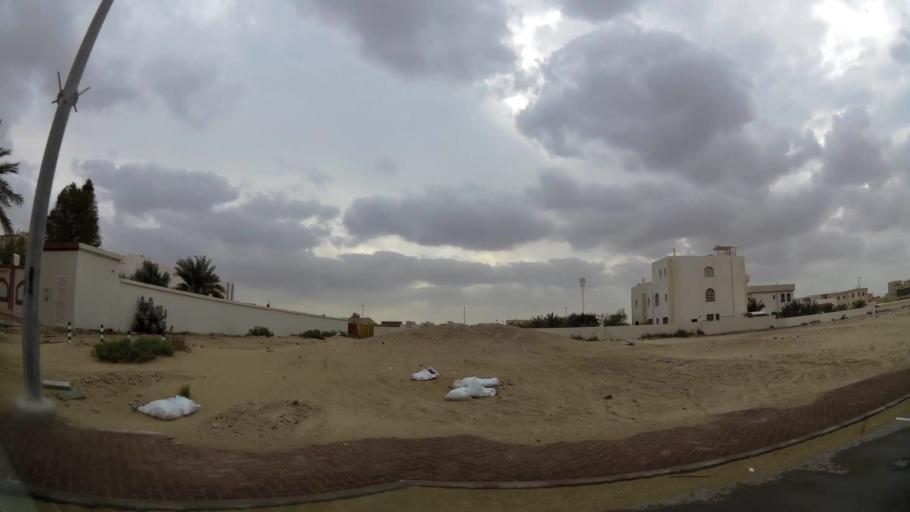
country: AE
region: Abu Dhabi
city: Abu Dhabi
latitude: 24.3497
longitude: 54.6331
